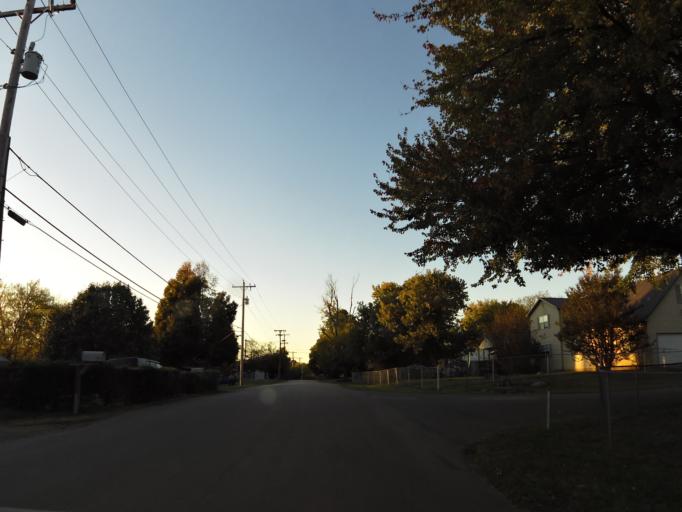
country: US
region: Tennessee
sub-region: Blount County
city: Alcoa
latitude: 35.7889
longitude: -83.9562
